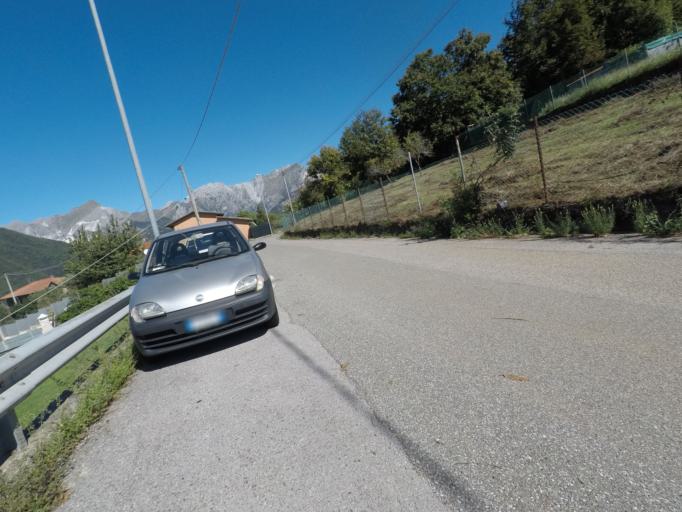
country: IT
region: Tuscany
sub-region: Provincia di Massa-Carrara
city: Montignoso
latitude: 44.0391
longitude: 10.1611
